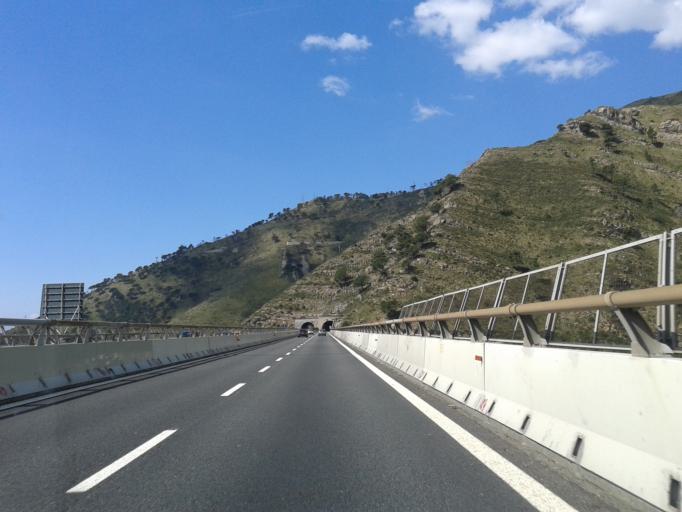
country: IT
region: Liguria
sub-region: Provincia di Genova
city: Bogliasco
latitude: 44.3927
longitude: 9.0431
